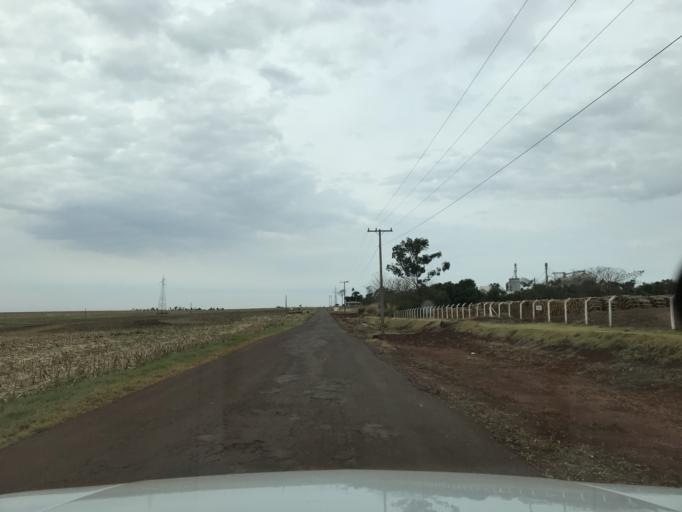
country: BR
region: Parana
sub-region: Palotina
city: Palotina
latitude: -24.2848
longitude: -53.7967
